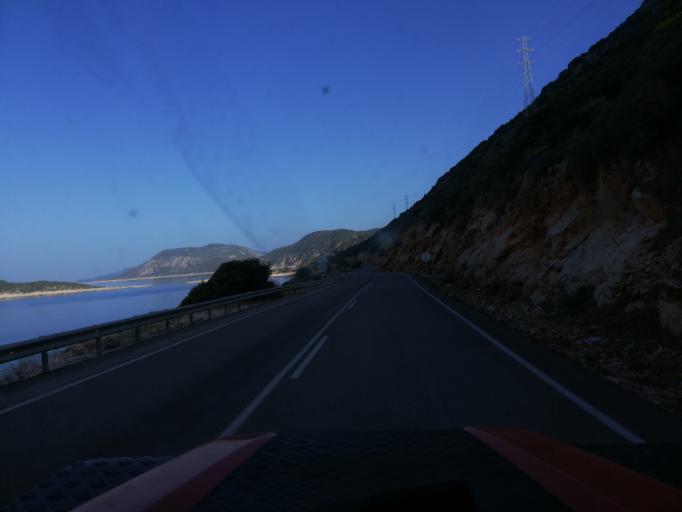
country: TR
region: Antalya
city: Kalkan
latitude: 36.2169
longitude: 29.4676
